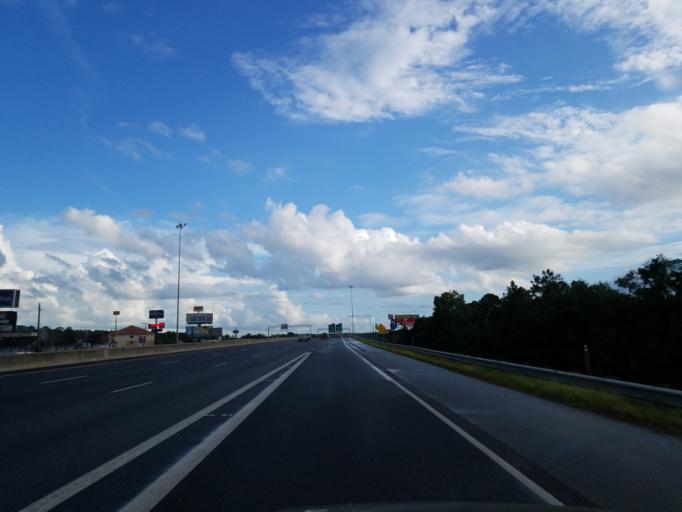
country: US
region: Georgia
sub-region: Tift County
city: Tifton
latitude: 31.4545
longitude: -83.5291
